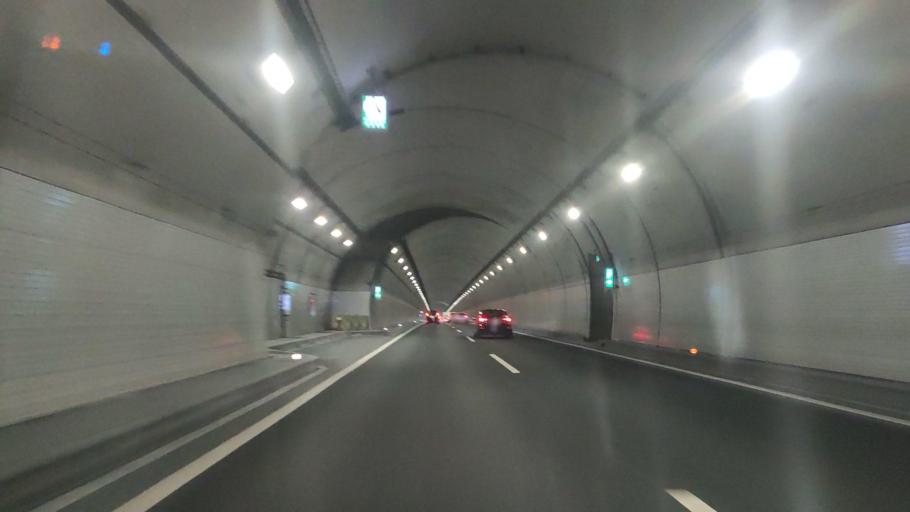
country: JP
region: Fukuoka
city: Kanda
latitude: 33.8092
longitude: 130.9146
